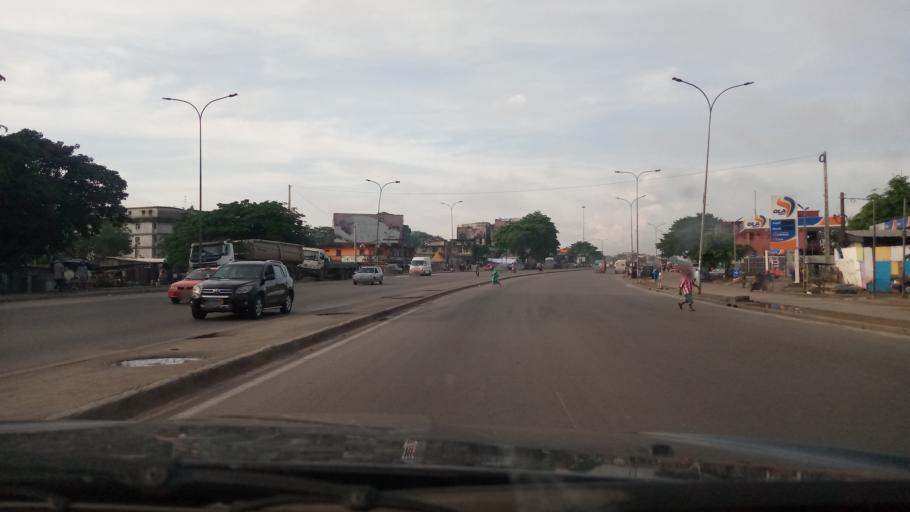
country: CI
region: Lagunes
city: Abobo
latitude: 5.4156
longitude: -4.0163
